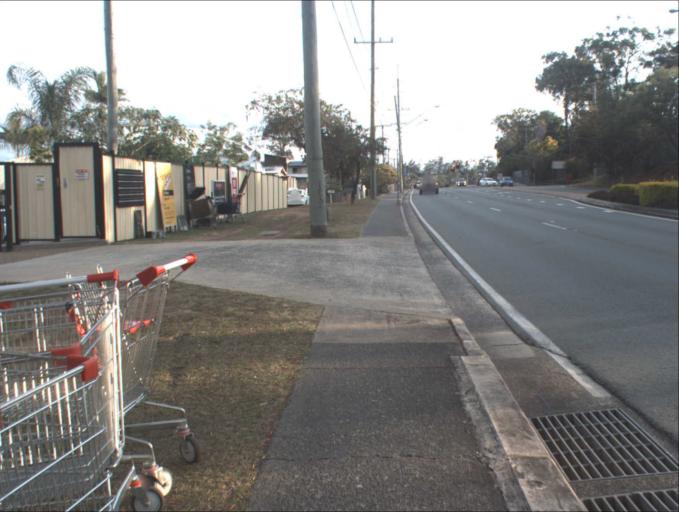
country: AU
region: Queensland
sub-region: Logan
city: Logan City
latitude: -27.6529
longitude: 153.1183
